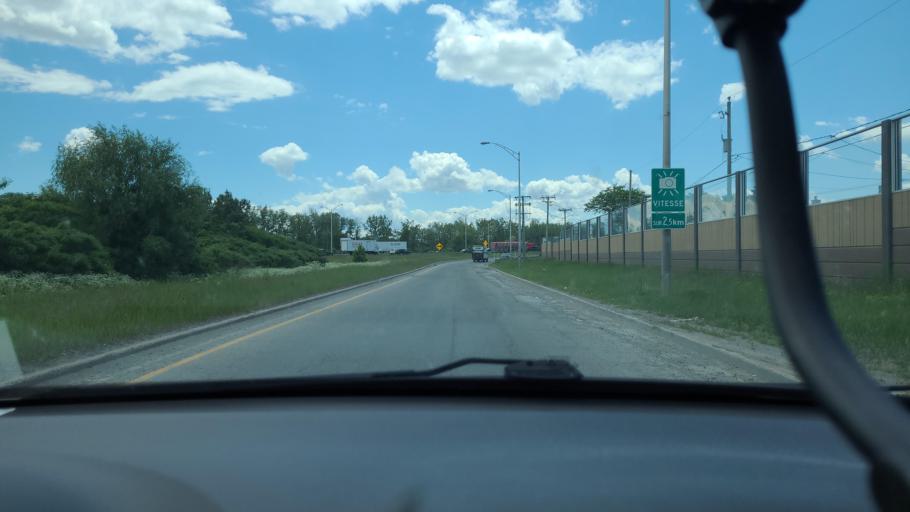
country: CA
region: Quebec
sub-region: Laval
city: Laval
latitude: 45.5931
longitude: -73.7200
